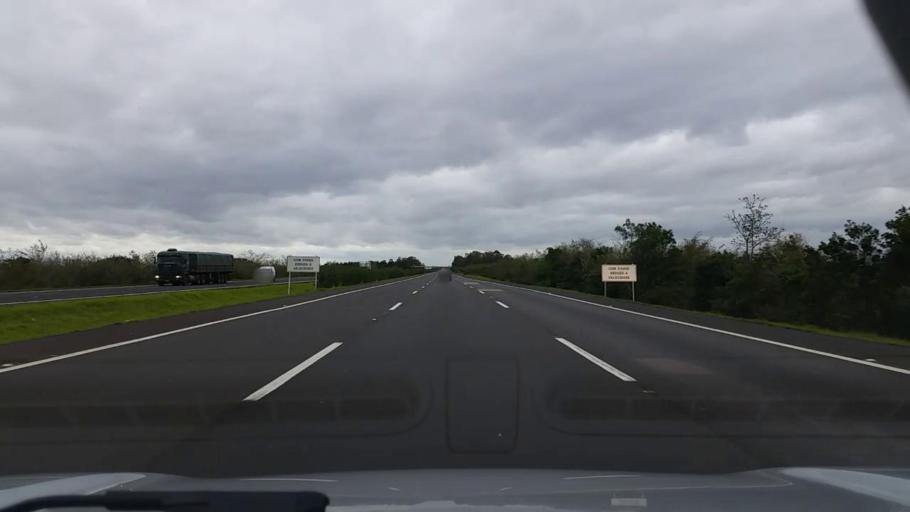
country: BR
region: Rio Grande do Sul
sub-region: Rolante
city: Rolante
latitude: -29.8841
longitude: -50.5679
